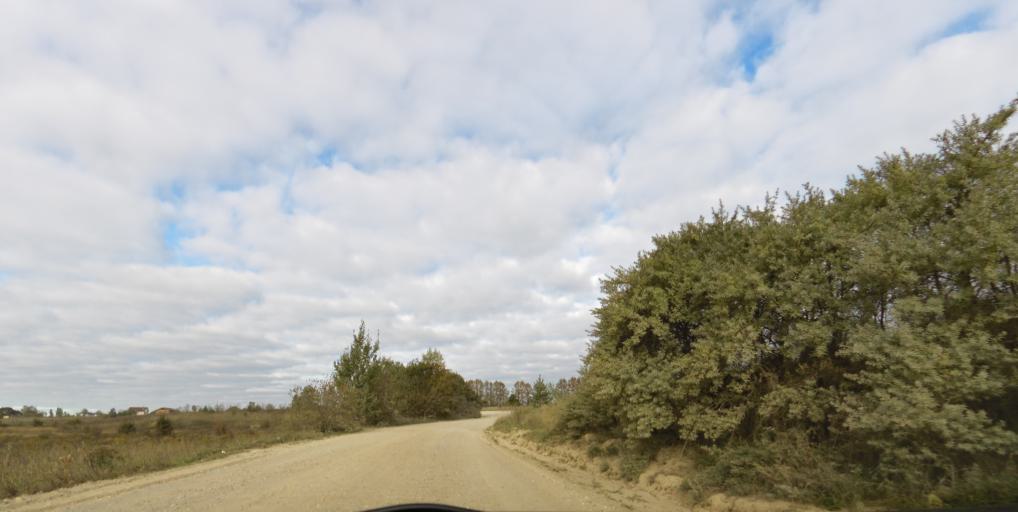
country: LT
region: Vilnius County
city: Pilaite
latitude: 54.7313
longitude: 25.1625
